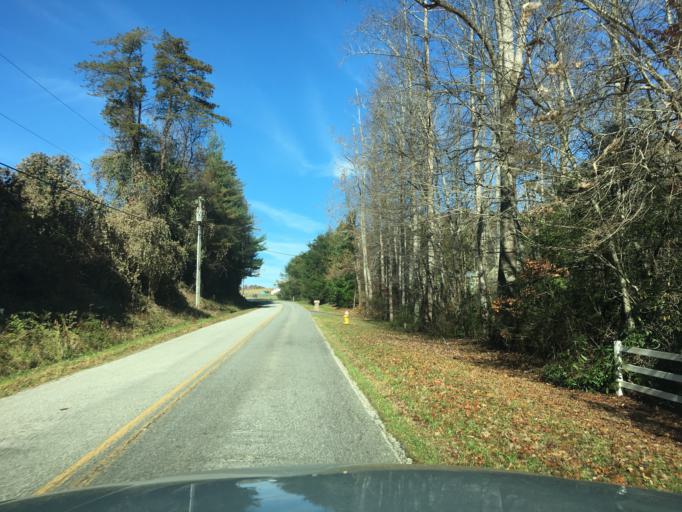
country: US
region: North Carolina
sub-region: Henderson County
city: Etowah
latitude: 35.3252
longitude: -82.6150
